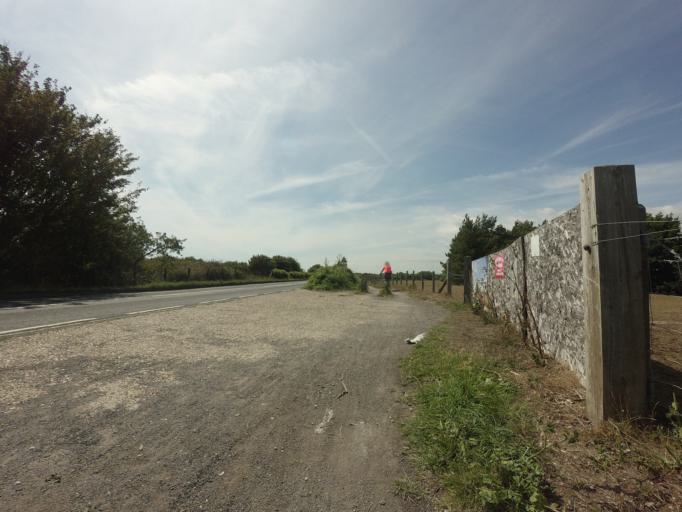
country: GB
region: England
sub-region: East Sussex
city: Rye
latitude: 50.9442
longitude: 0.7651
